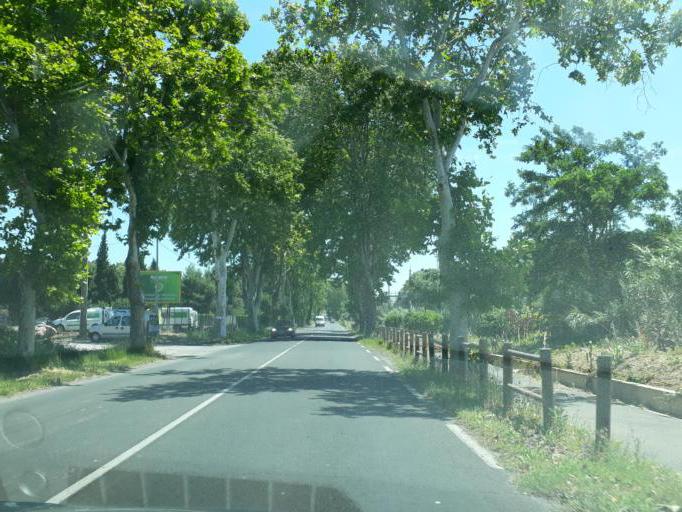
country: FR
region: Languedoc-Roussillon
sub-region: Departement de l'Herault
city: Beziers
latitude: 43.3300
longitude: 3.2409
